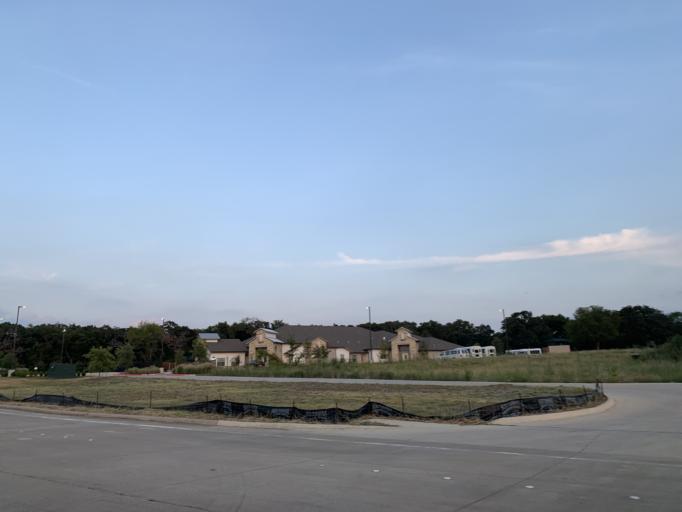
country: US
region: Texas
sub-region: Tarrant County
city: Keller
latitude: 32.9551
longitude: -97.2763
